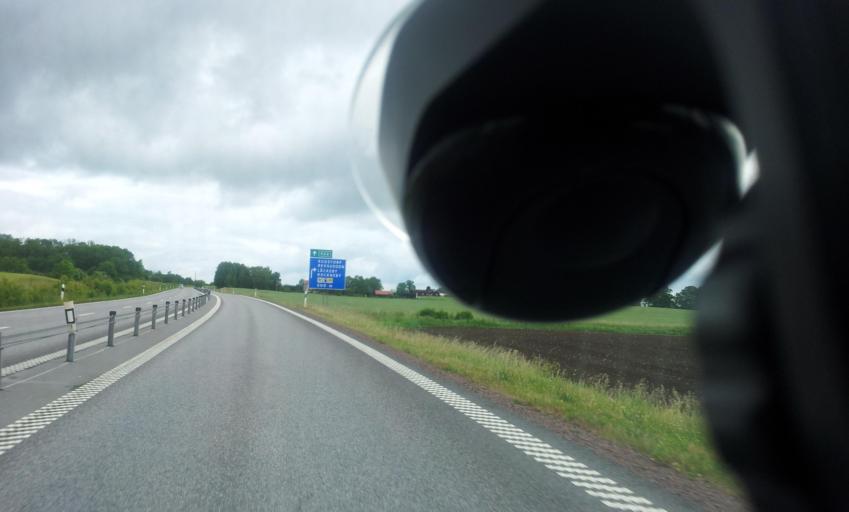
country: SE
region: Kalmar
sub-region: Kalmar Kommun
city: Lindsdal
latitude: 56.7845
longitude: 16.3428
